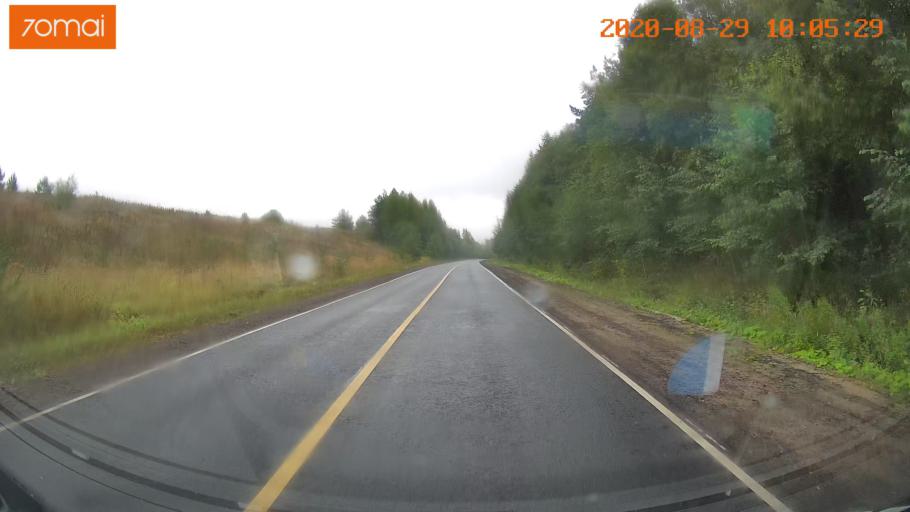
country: RU
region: Ivanovo
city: Zarechnyy
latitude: 57.3926
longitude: 42.5228
